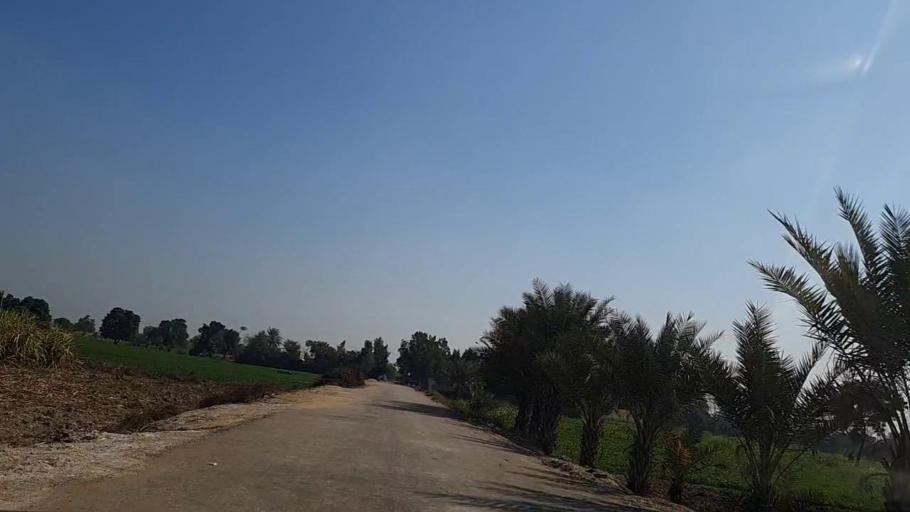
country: PK
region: Sindh
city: Sakrand
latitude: 26.2291
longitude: 68.3080
